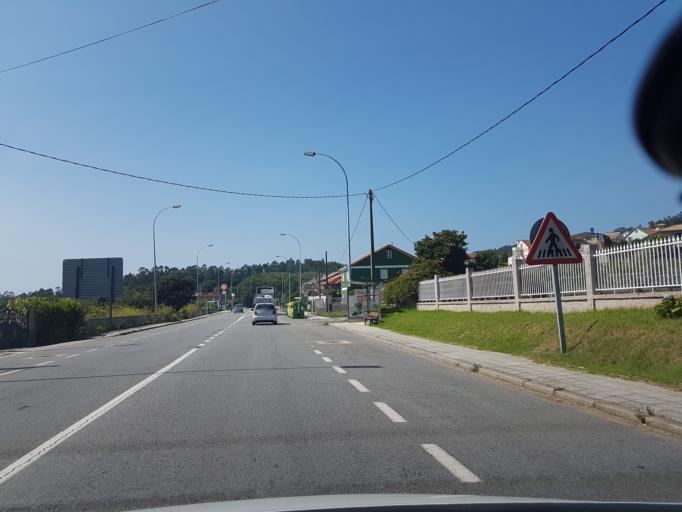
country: ES
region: Galicia
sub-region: Provincia de Pontevedra
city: Redondela
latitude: 42.2326
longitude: -8.6417
